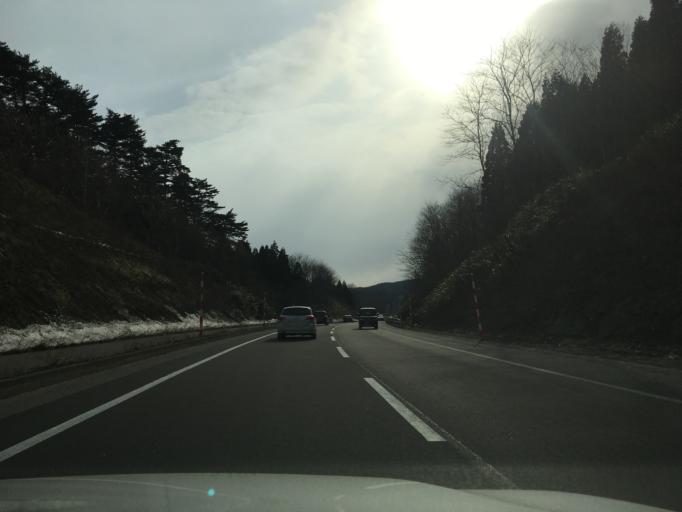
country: JP
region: Aomori
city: Namioka
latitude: 40.7708
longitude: 140.5974
